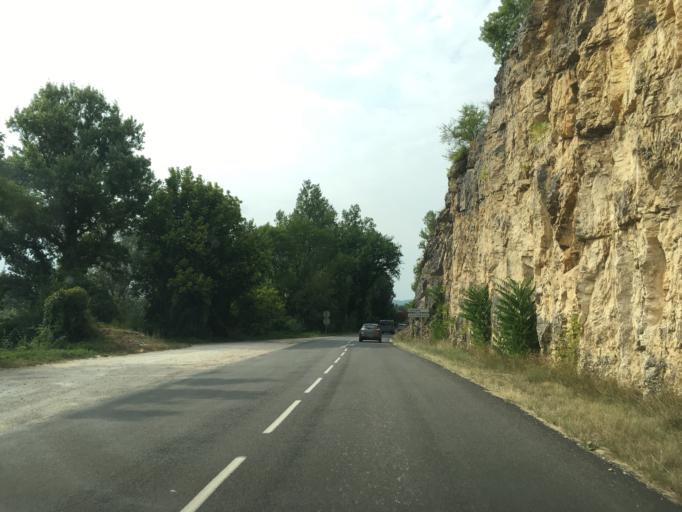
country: FR
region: Midi-Pyrenees
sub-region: Departement du Lot
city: Souillac
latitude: 44.8816
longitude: 1.4884
